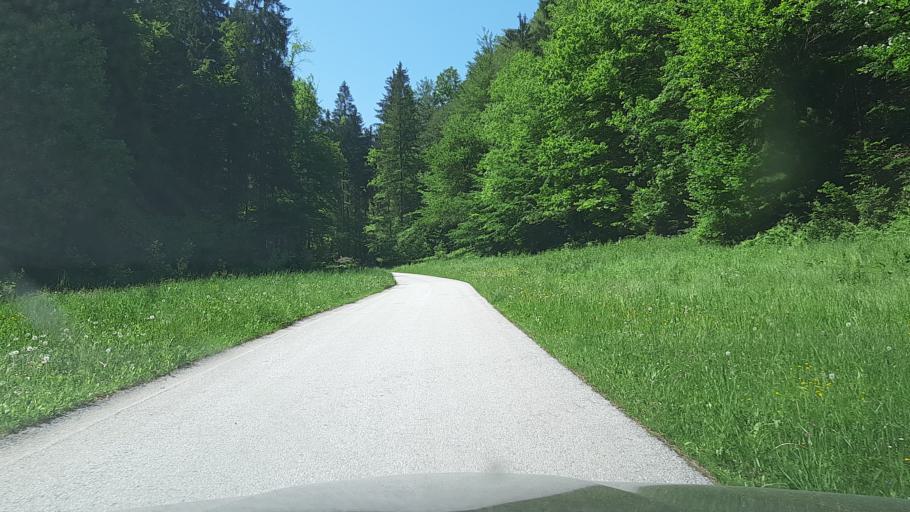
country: SI
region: Skofja Loka
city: Skofja Loka
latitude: 46.1267
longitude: 14.2795
